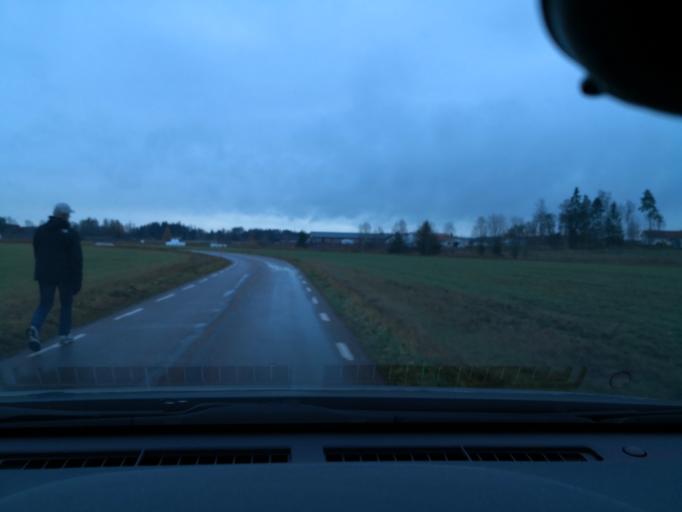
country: SE
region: Vaestmanland
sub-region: Hallstahammars Kommun
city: Kolback
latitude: 59.5617
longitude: 16.2032
